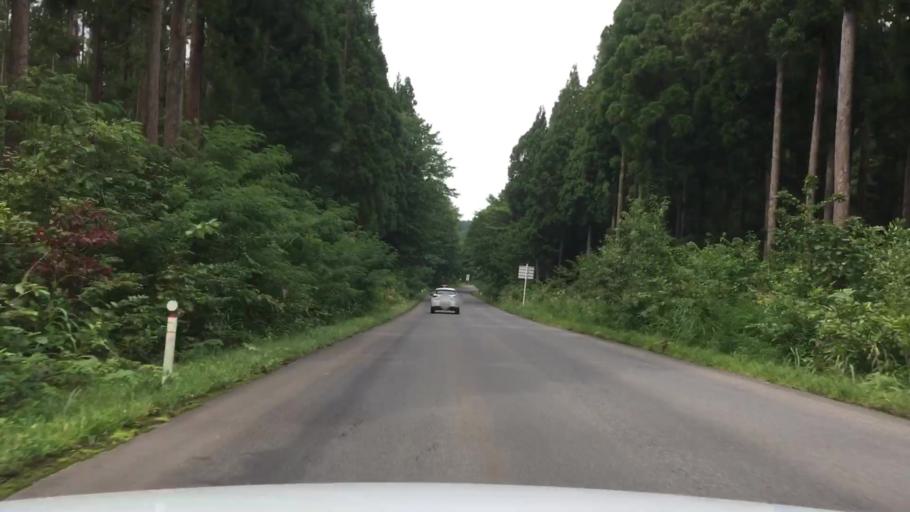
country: JP
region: Aomori
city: Shimokizukuri
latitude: 40.7119
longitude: 140.2683
